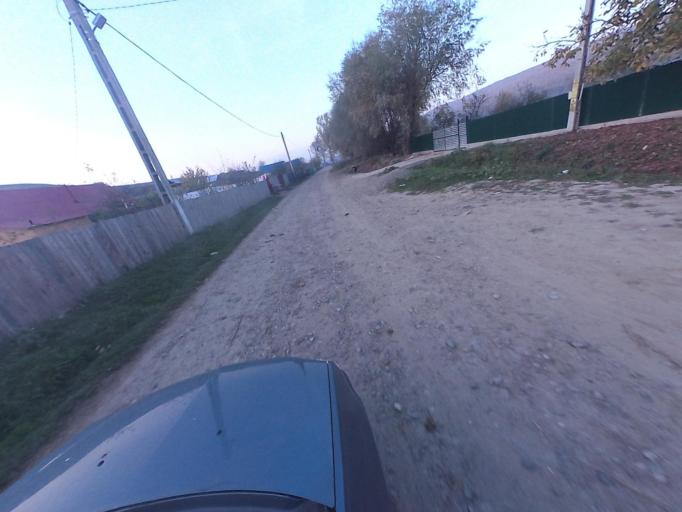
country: RO
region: Vaslui
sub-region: Comuna Garceni
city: Garceni
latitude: 46.7920
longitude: 27.2421
